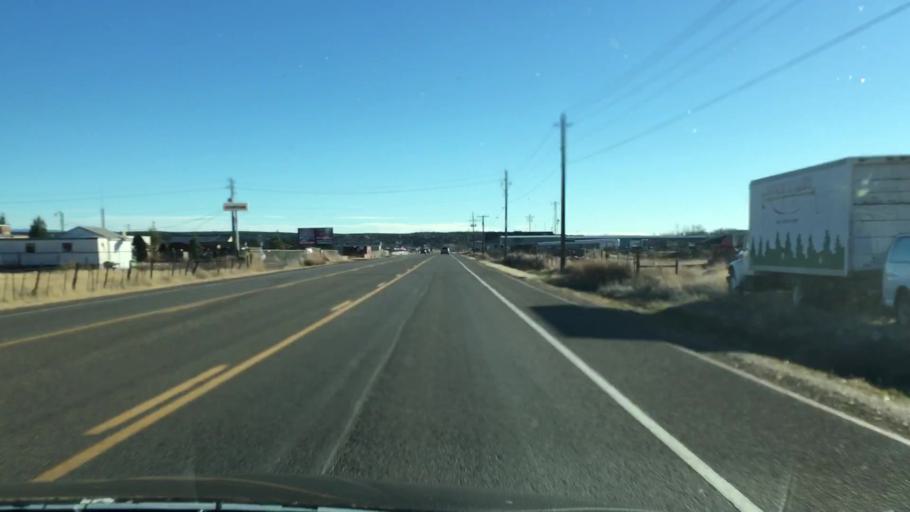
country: US
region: Utah
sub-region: Kane County
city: Kanab
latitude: 37.0197
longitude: -112.5250
